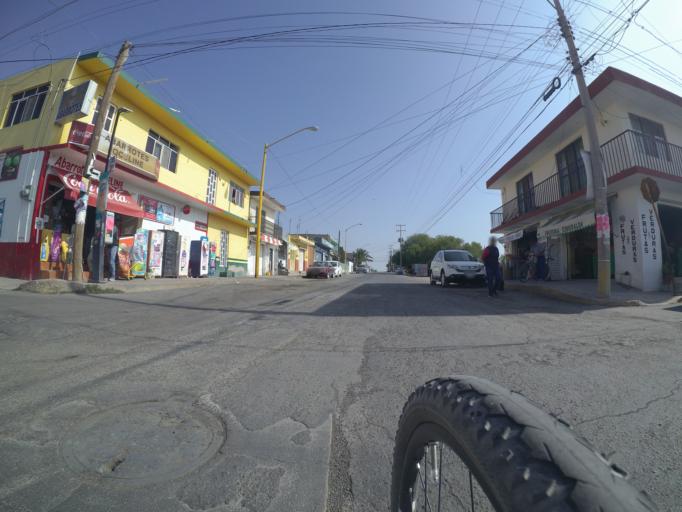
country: MX
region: Aguascalientes
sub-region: Jesus Maria
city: Jesus Maria
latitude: 21.9654
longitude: -102.3424
